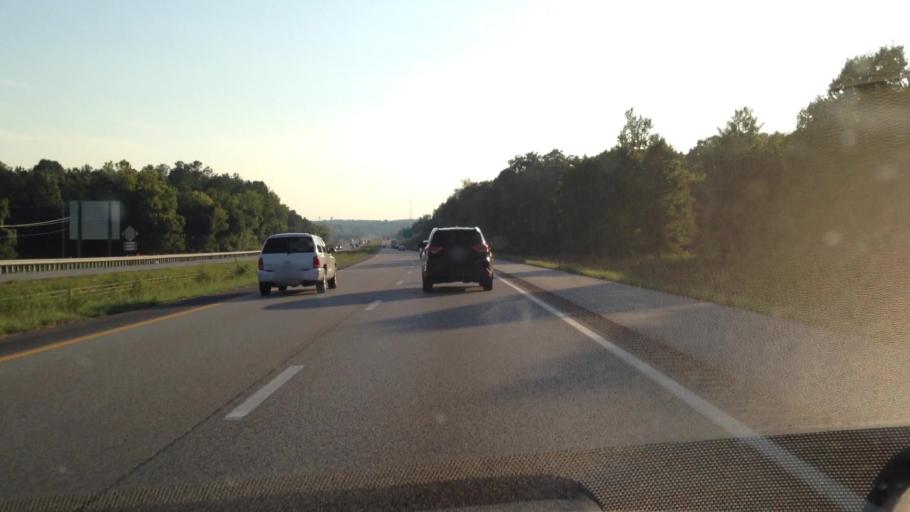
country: US
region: Missouri
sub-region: Jasper County
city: Joplin
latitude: 37.0430
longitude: -94.5048
